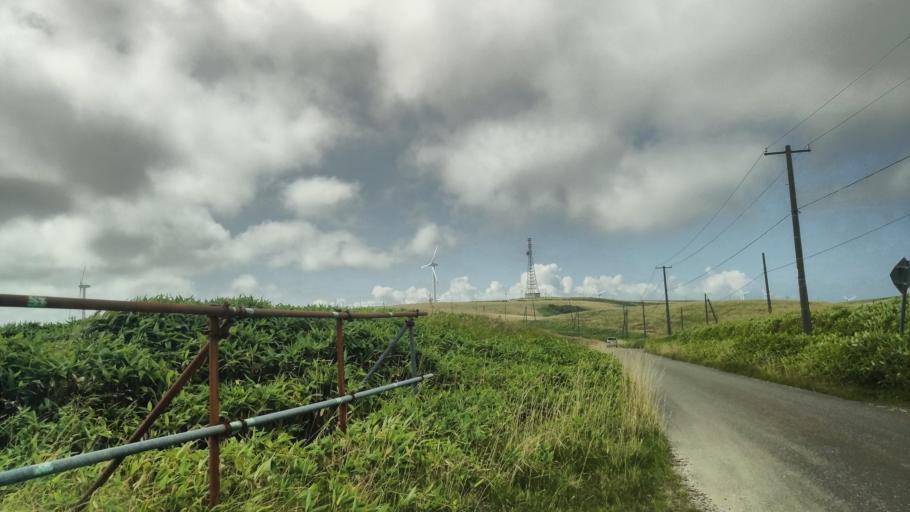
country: JP
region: Hokkaido
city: Makubetsu
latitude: 45.4834
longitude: 141.9269
